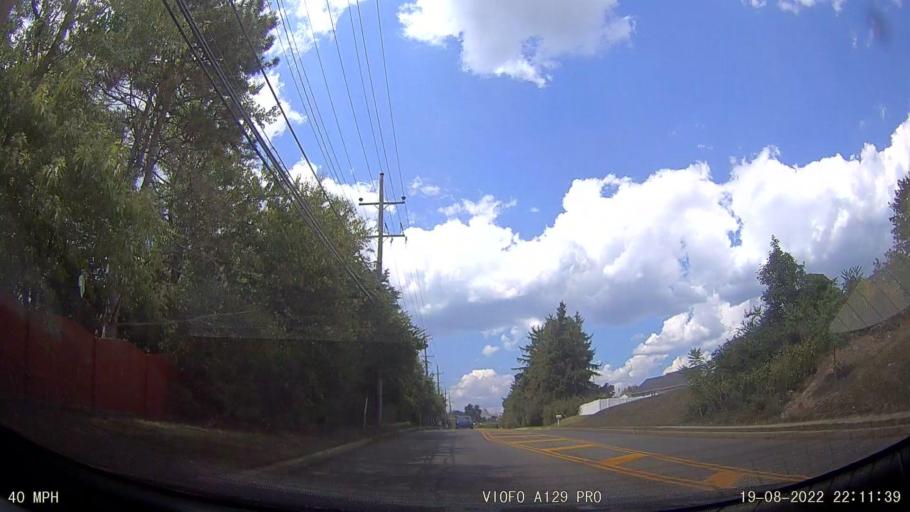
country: US
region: Pennsylvania
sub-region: Montgomery County
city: Bridgeport
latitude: 40.0983
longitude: -75.3670
